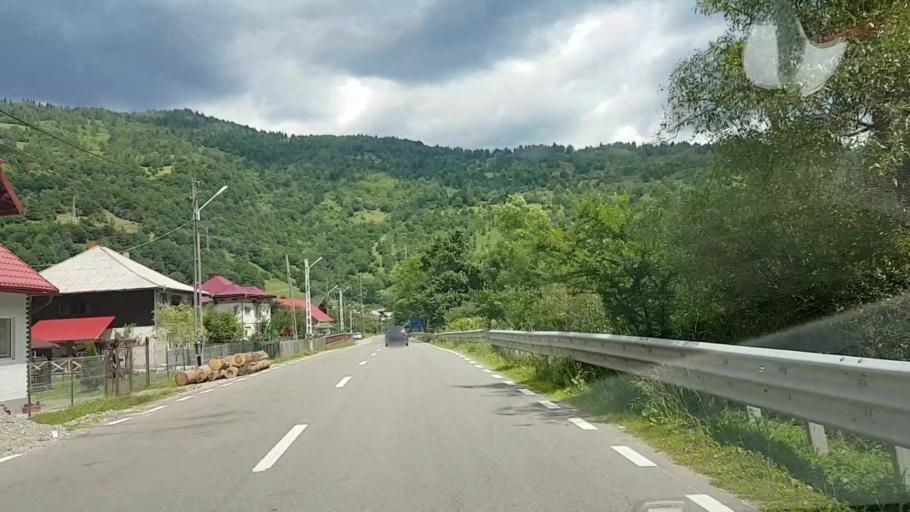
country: RO
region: Suceava
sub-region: Comuna Brosteni
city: Brosteni
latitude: 47.2581
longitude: 25.6799
